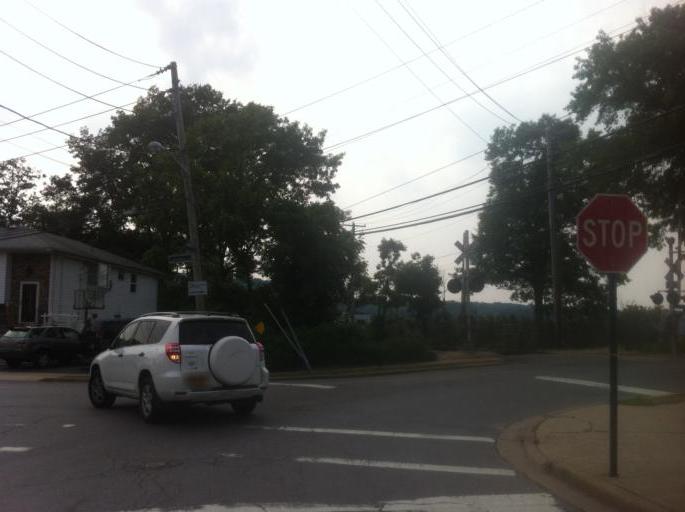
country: US
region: New York
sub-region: Nassau County
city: Oyster Bay
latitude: 40.8752
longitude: -73.5359
